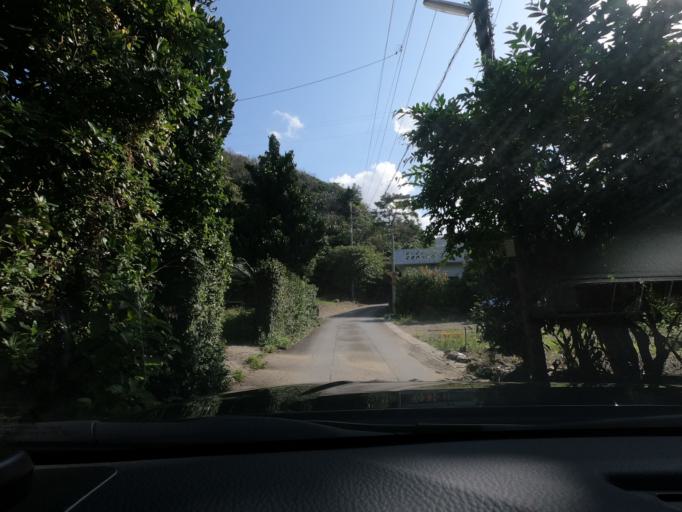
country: JP
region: Okinawa
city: Nago
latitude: 26.7574
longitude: 128.1920
